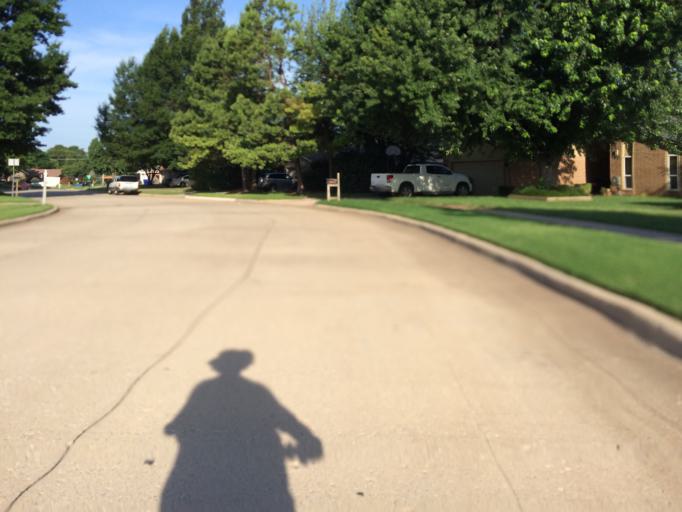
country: US
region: Oklahoma
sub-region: Cleveland County
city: Norman
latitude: 35.2244
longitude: -97.4921
